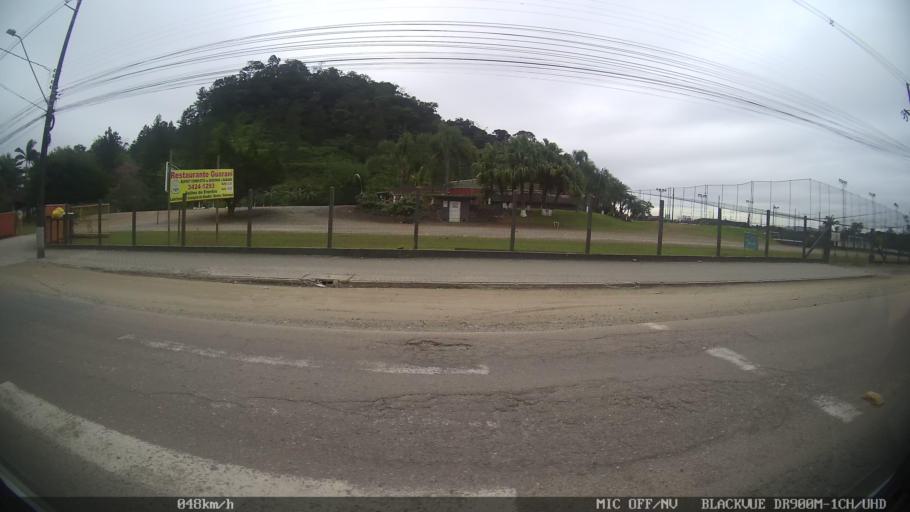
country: BR
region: Santa Catarina
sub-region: Joinville
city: Joinville
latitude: -26.2154
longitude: -48.9049
